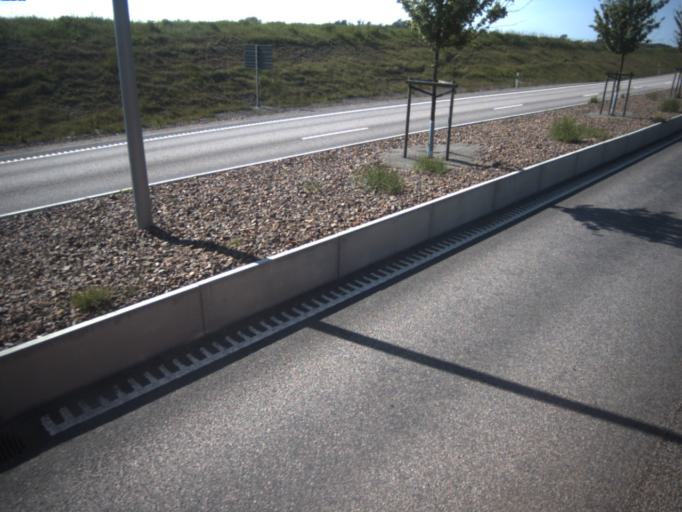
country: SE
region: Skane
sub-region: Helsingborg
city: Gantofta
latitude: 56.0342
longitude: 12.7611
